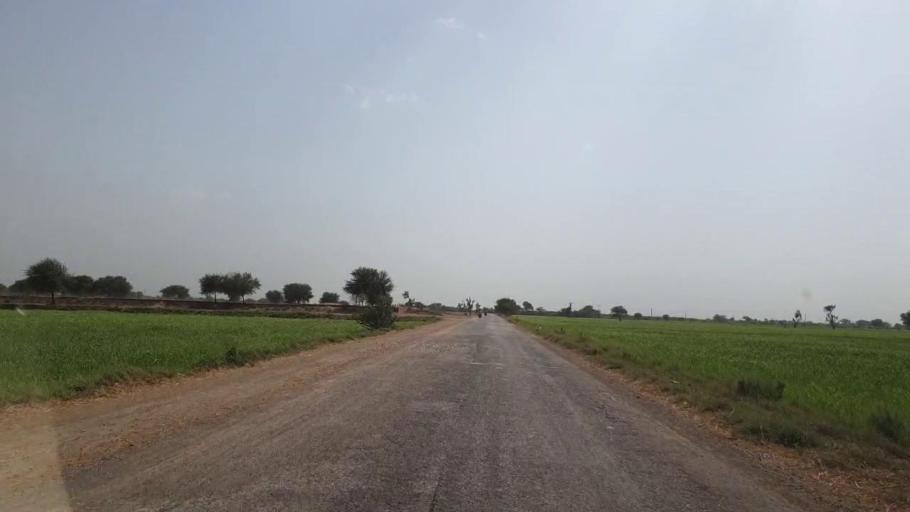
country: PK
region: Sindh
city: Tando Ghulam Ali
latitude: 25.0699
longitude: 68.8230
